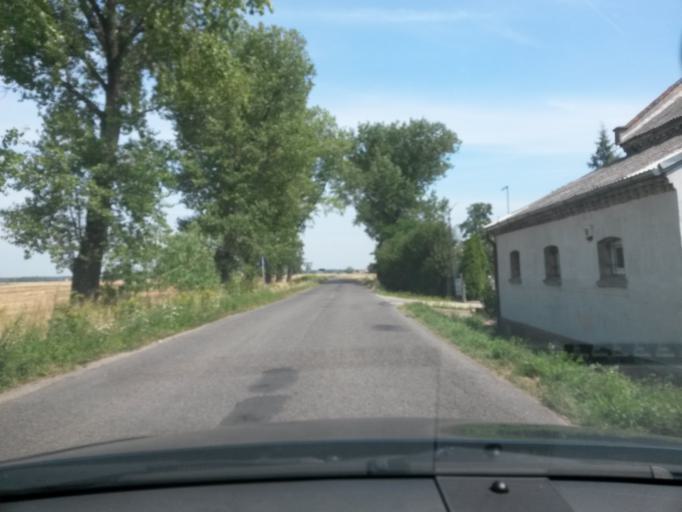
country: PL
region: Lower Silesian Voivodeship
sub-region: Powiat legnicki
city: Prochowice
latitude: 51.1983
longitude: 16.3456
